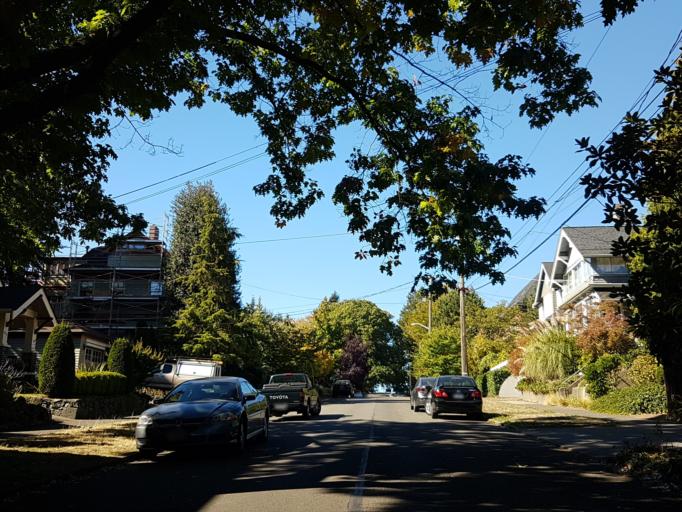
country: US
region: Washington
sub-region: King County
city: Seattle
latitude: 47.6313
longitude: -122.3620
